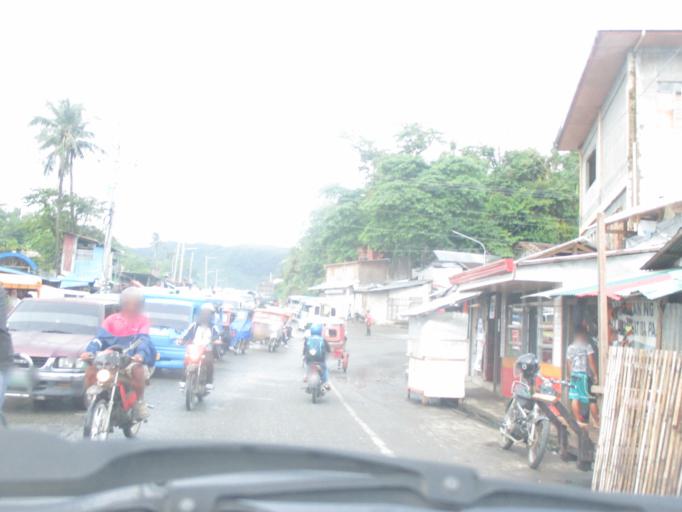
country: PH
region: Eastern Visayas
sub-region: Province of Leyte
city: Panalanoy
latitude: 11.2464
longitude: 124.9950
